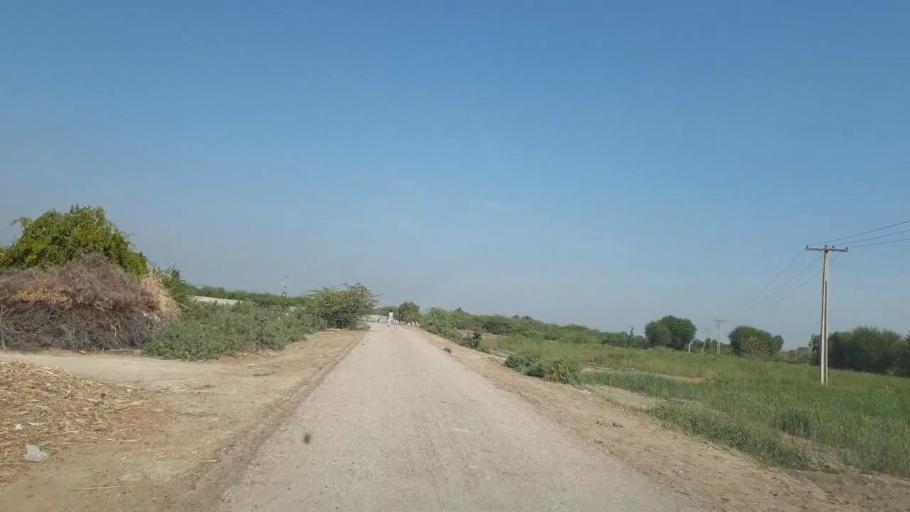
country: PK
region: Sindh
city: Mirpur Khas
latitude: 25.6230
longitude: 69.0875
